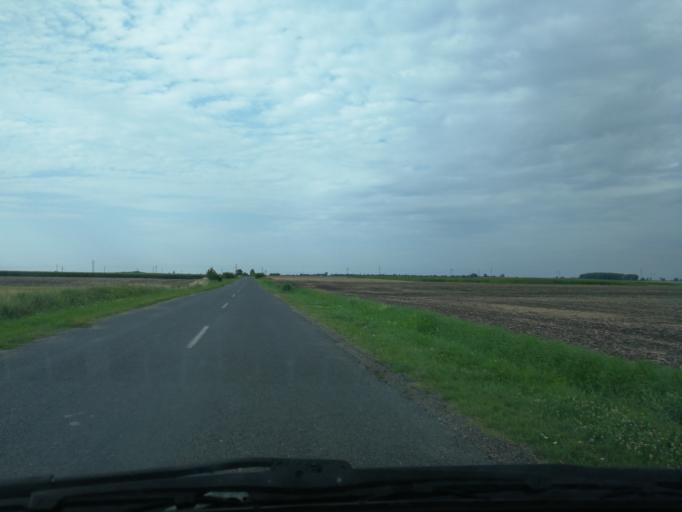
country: HU
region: Bacs-Kiskun
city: Kalocsa
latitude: 46.4899
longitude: 19.0517
